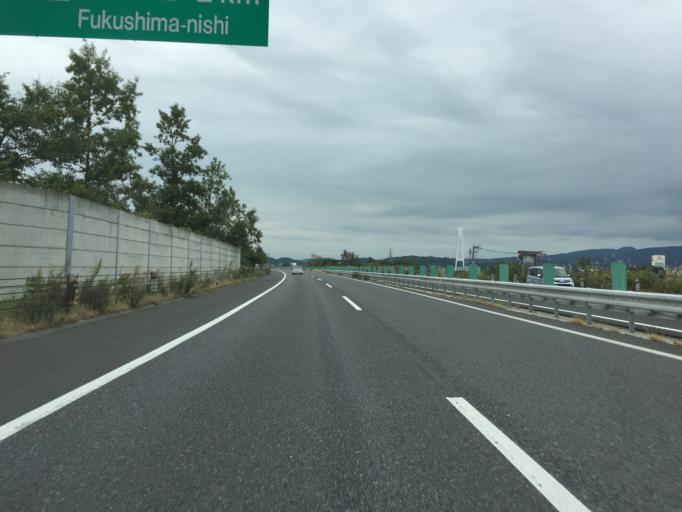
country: JP
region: Fukushima
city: Fukushima-shi
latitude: 37.7532
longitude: 140.4090
